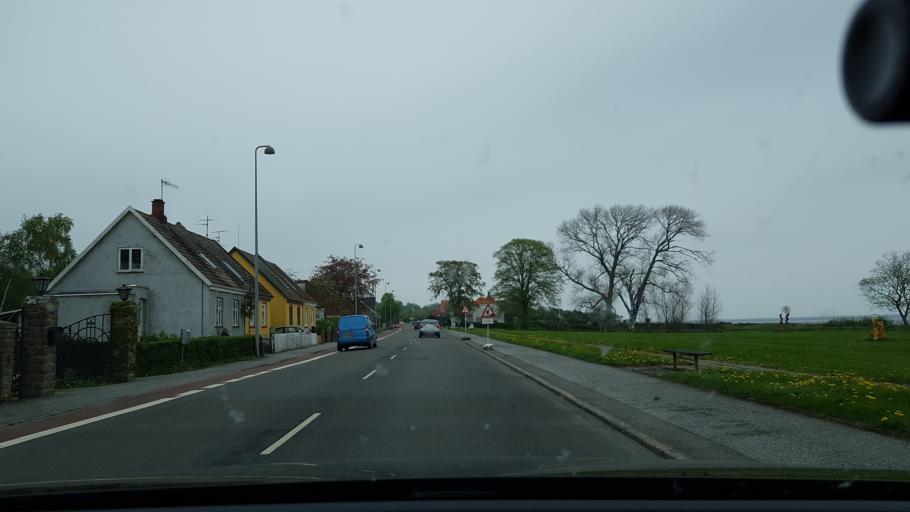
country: DK
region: Capital Region
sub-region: Bornholm Kommune
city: Nexo
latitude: 55.0699
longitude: 15.1379
